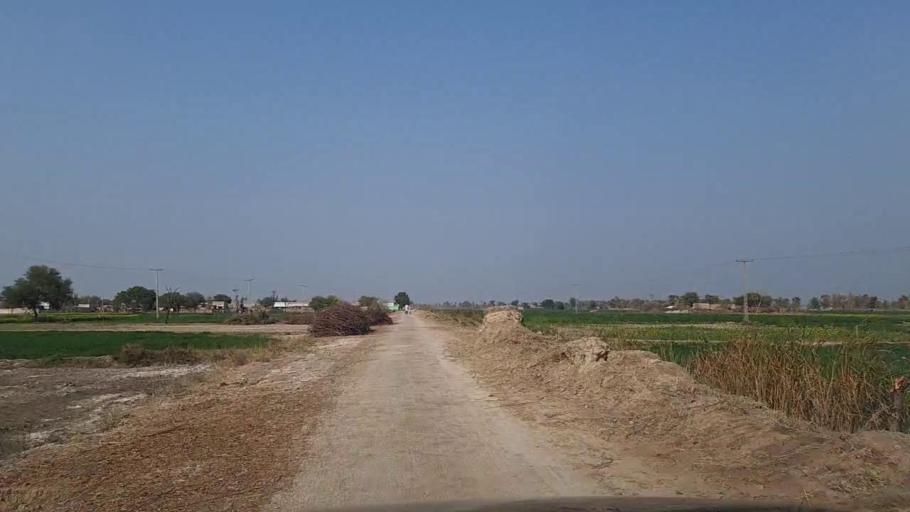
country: PK
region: Sindh
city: Daur
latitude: 26.4079
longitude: 68.4188
